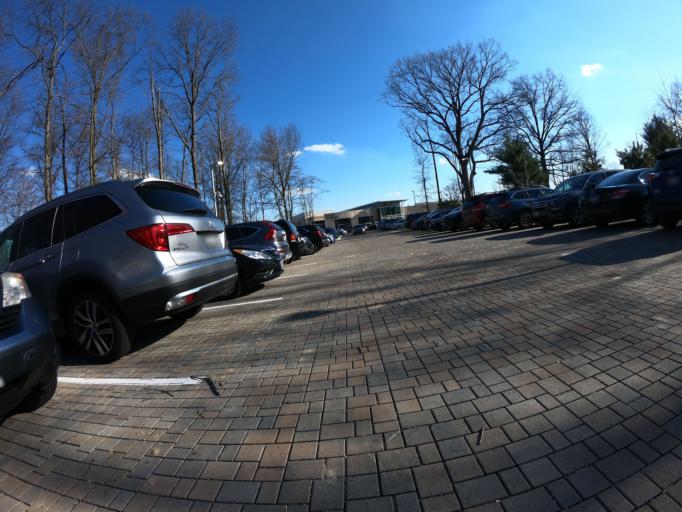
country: US
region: Maryland
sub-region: Howard County
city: West Elkridge
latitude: 39.2025
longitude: -76.7368
